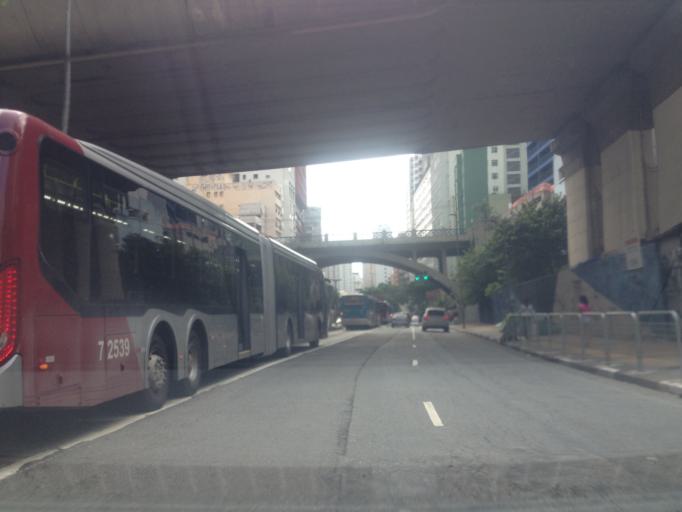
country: BR
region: Sao Paulo
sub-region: Sao Paulo
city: Sao Paulo
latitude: -23.5515
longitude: -46.6466
